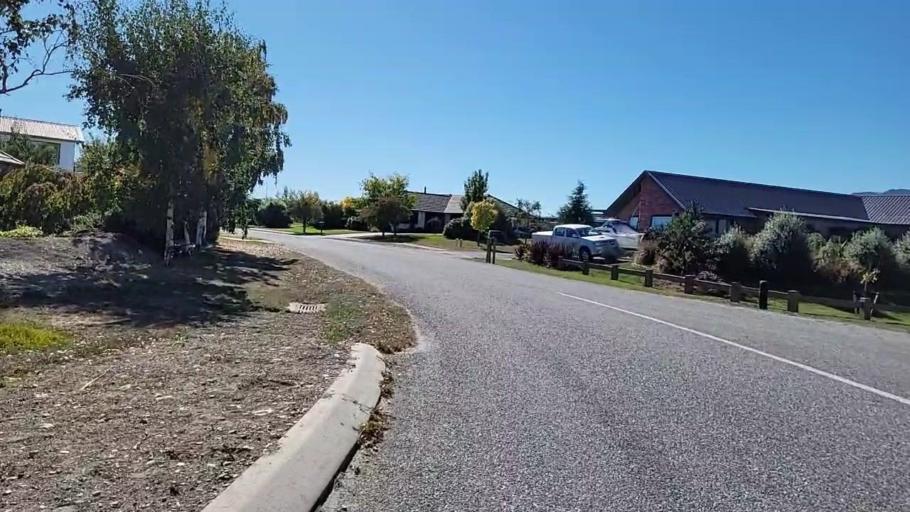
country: NZ
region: Otago
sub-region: Queenstown-Lakes District
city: Wanaka
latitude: -44.9735
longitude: 169.2459
